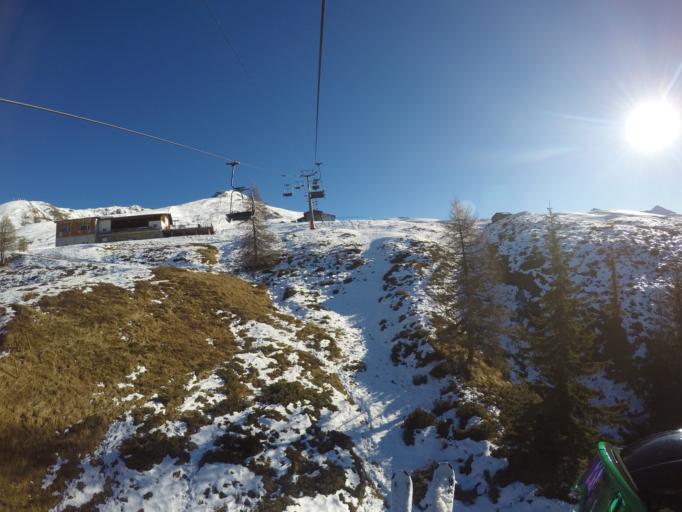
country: CH
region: Grisons
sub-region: Praettigau/Davos District
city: Davos
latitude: 46.7785
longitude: 9.8306
